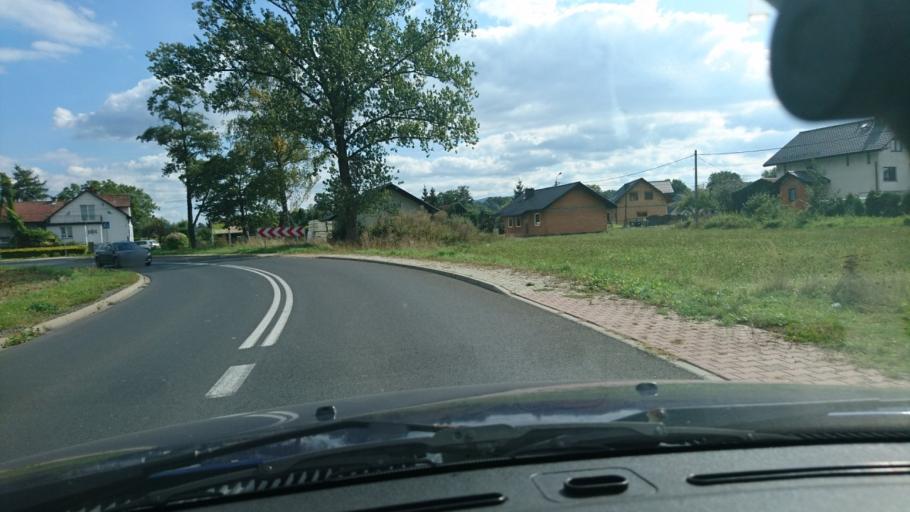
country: PL
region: Silesian Voivodeship
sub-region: Powiat bielski
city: Mazancowice
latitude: 49.8679
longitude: 18.9644
